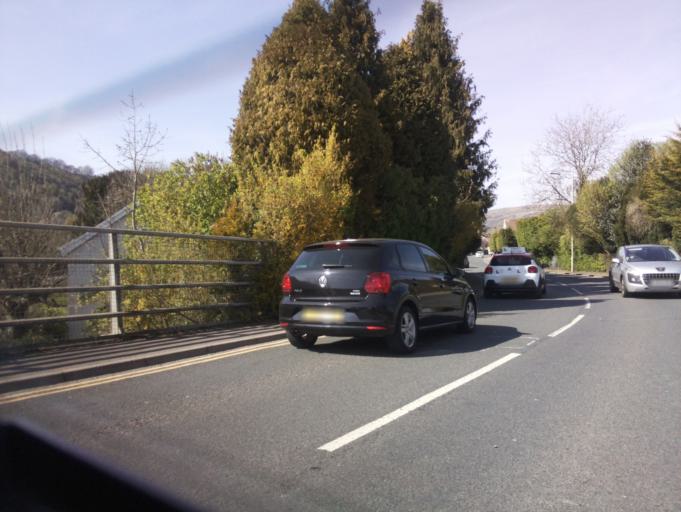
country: GB
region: Wales
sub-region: Cardiff
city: Pentyrch
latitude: 51.5473
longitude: -3.2710
